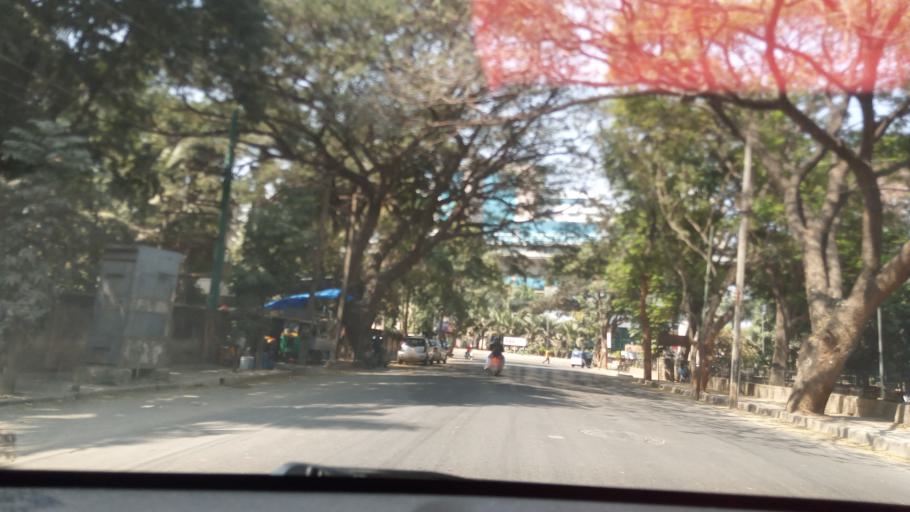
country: IN
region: Karnataka
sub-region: Bangalore Urban
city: Bangalore
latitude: 12.9922
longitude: 77.7060
